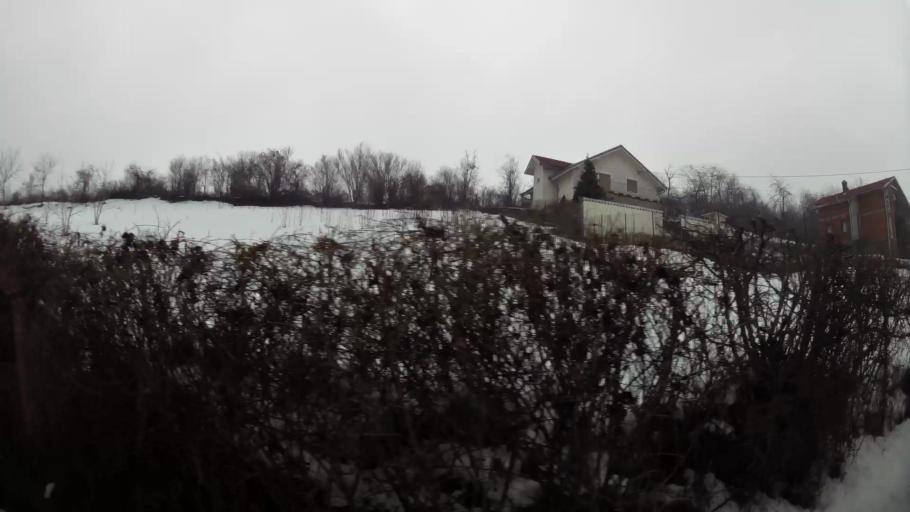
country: RS
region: Central Serbia
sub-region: Belgrade
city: Zvezdara
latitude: 44.7483
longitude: 20.5180
